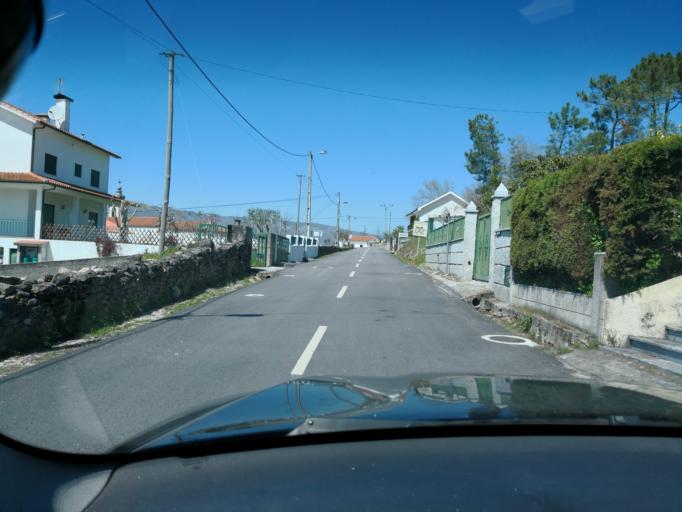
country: PT
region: Vila Real
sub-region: Vila Real
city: Vila Real
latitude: 41.3127
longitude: -7.6944
